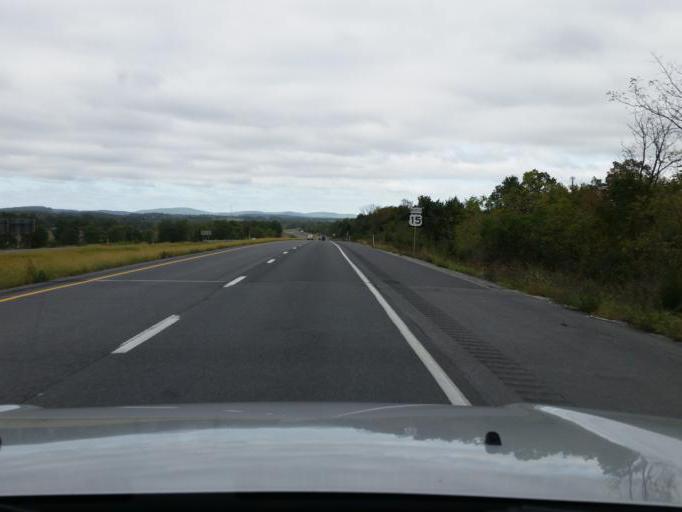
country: US
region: Pennsylvania
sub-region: Adams County
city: Lake Meade
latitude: 39.9544
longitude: -77.1329
